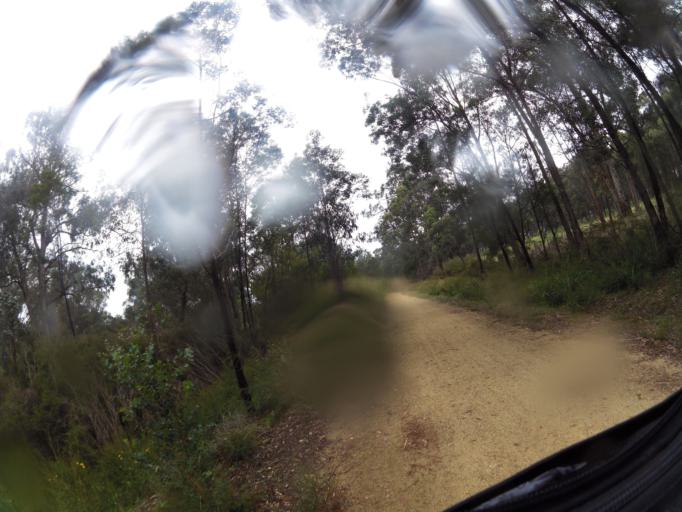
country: AU
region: Victoria
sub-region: East Gippsland
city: Lakes Entrance
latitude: -37.7528
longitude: 147.8126
